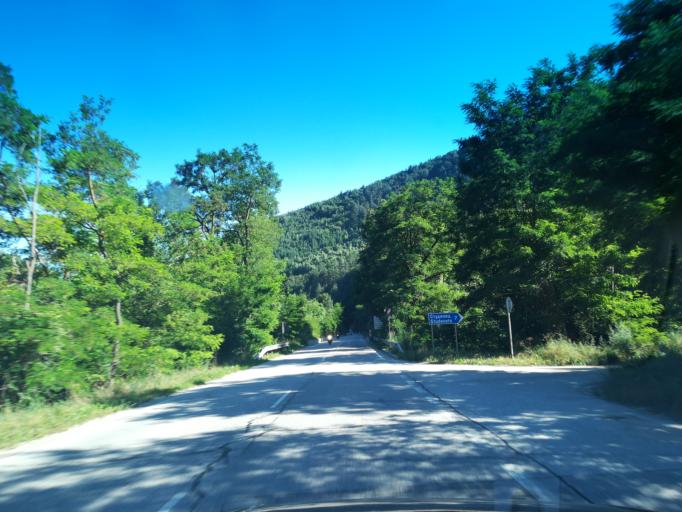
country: BG
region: Smolyan
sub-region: Obshtina Chepelare
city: Chepelare
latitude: 41.8394
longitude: 24.6795
